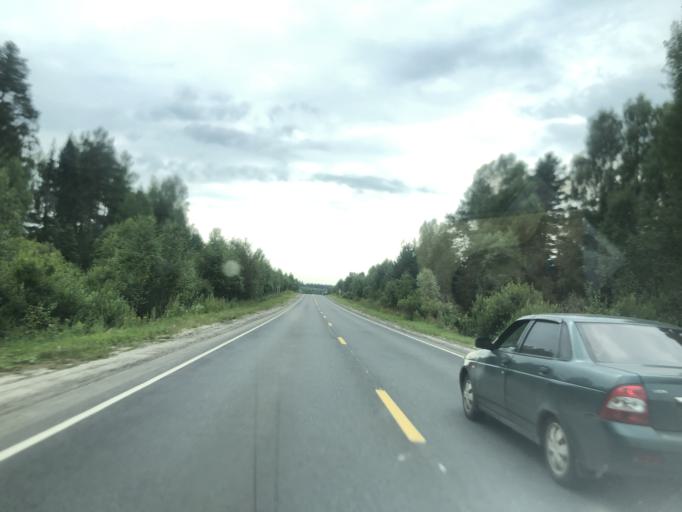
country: RU
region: Ivanovo
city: Pestyaki
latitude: 56.7056
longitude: 42.7494
